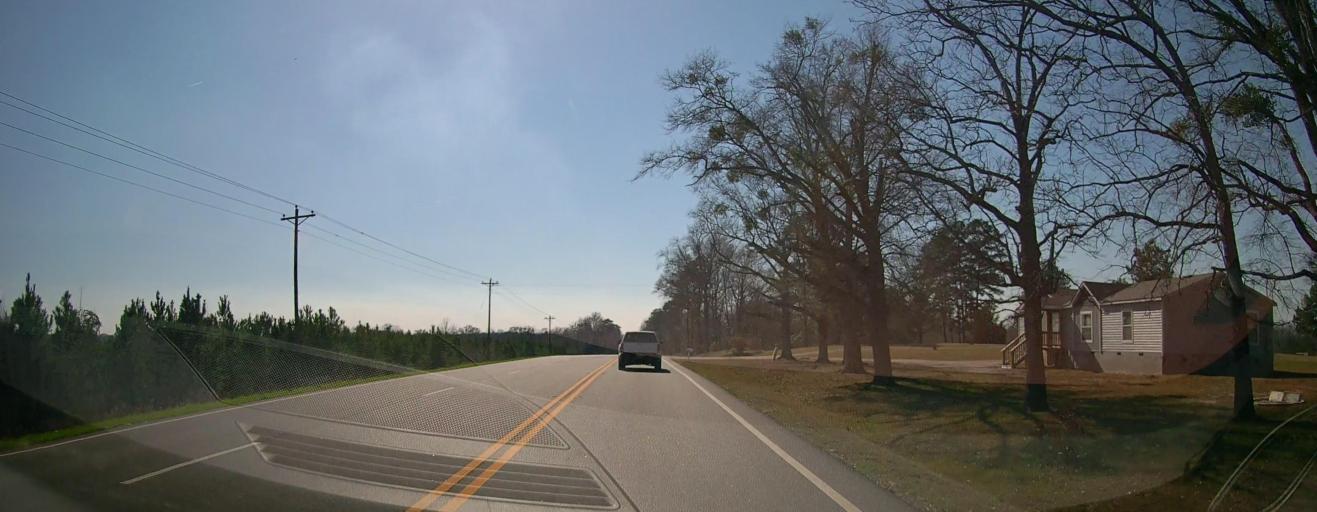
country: US
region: Georgia
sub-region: Macon County
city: Marshallville
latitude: 32.3286
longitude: -83.8718
